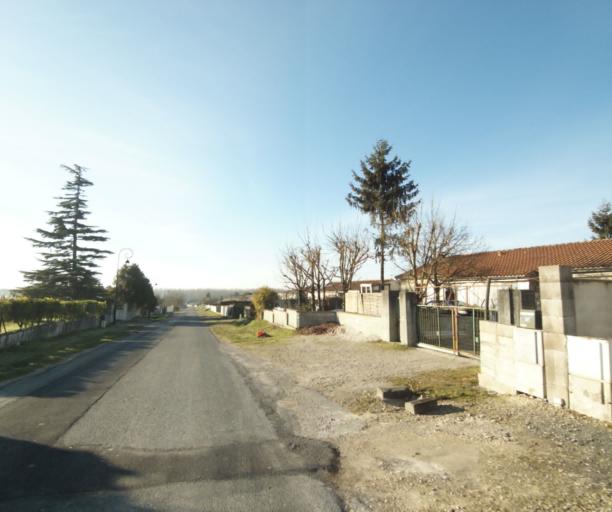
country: FR
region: Poitou-Charentes
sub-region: Departement de la Charente-Maritime
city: Cherac
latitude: 45.6904
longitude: -0.4501
